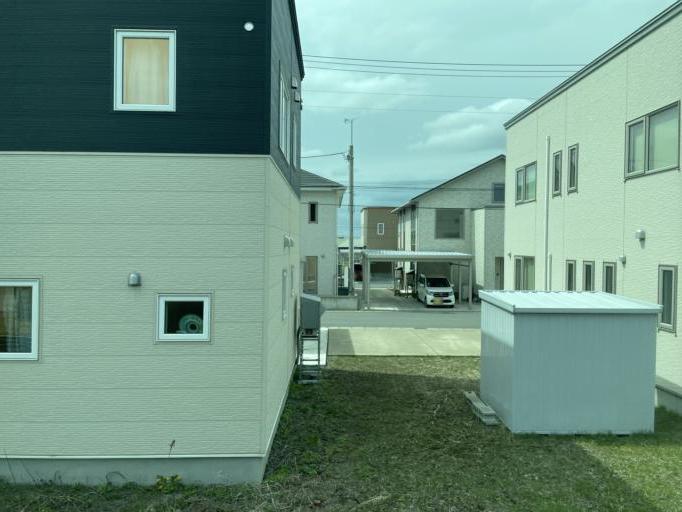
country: JP
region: Aomori
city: Goshogawara
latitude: 40.7594
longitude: 140.4357
